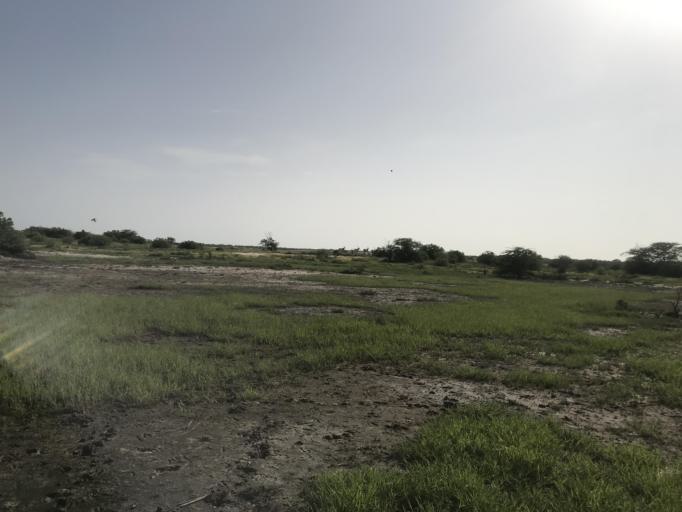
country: SN
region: Saint-Louis
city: Saint-Louis
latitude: 15.9297
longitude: -16.4602
